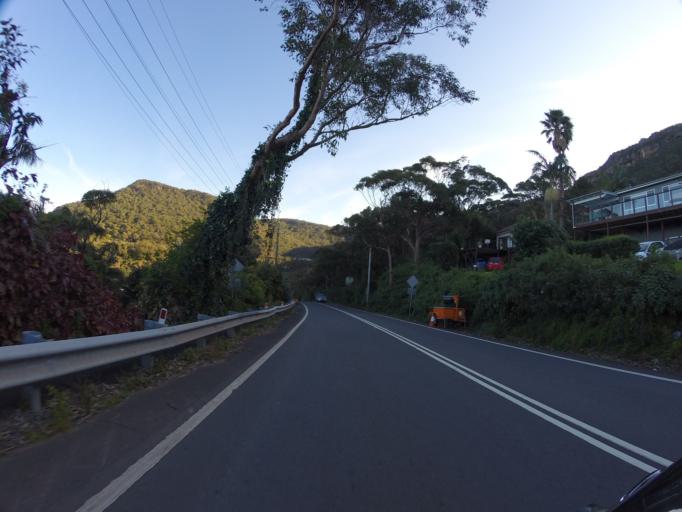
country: AU
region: New South Wales
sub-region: Wollongong
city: Helensburgh
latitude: -34.2432
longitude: 150.9766
